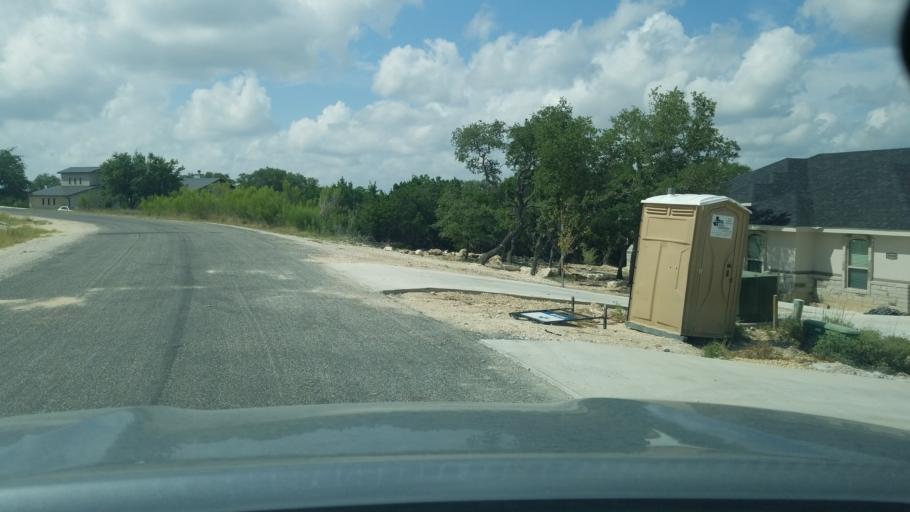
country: US
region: Texas
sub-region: Bexar County
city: Timberwood Park
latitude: 29.6853
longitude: -98.5207
